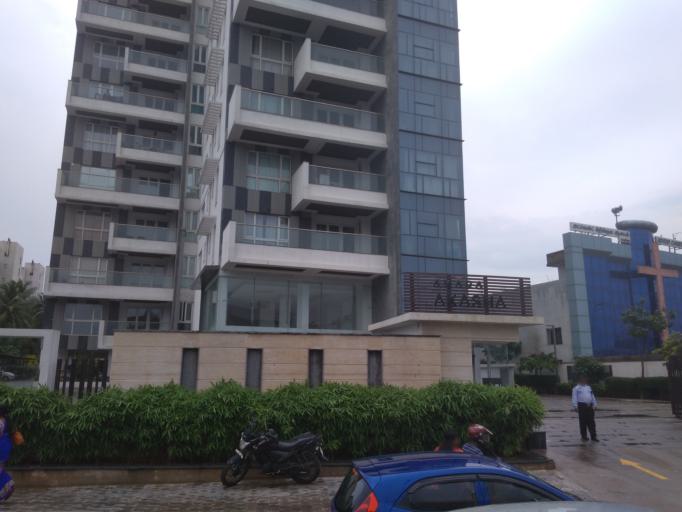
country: IN
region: Tamil Nadu
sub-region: Kancheepuram
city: Perungudi
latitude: 12.9635
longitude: 80.2464
